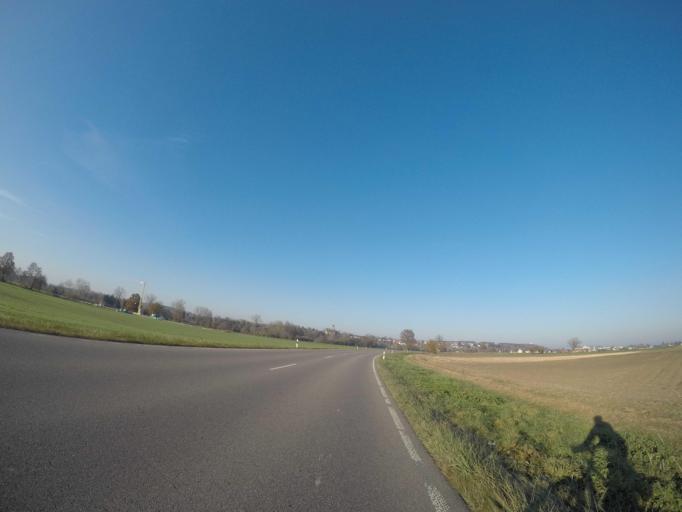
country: DE
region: Baden-Wuerttemberg
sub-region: Tuebingen Region
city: Rottenacker
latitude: 48.2225
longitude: 9.6854
